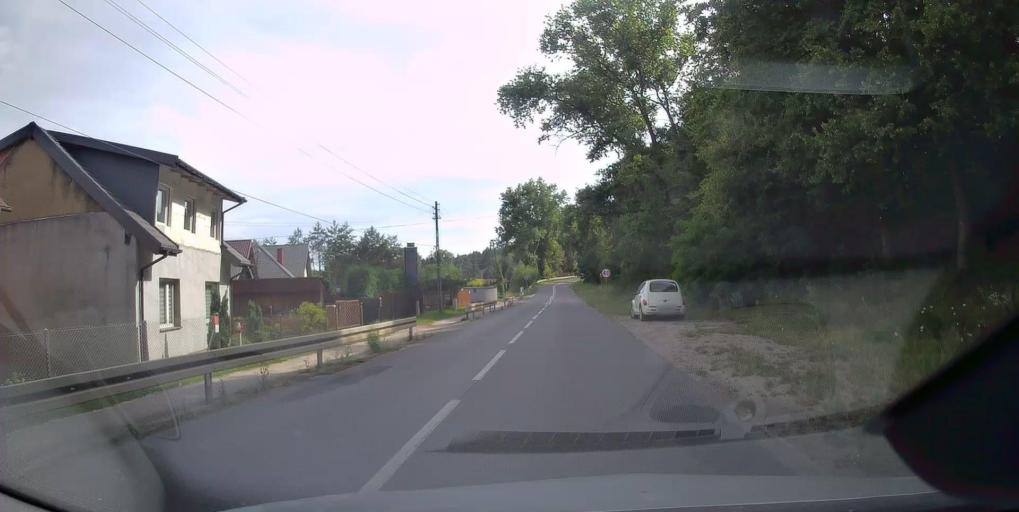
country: PL
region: Lodz Voivodeship
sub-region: Powiat tomaszowski
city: Tomaszow Mazowiecki
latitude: 51.4961
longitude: 19.9943
